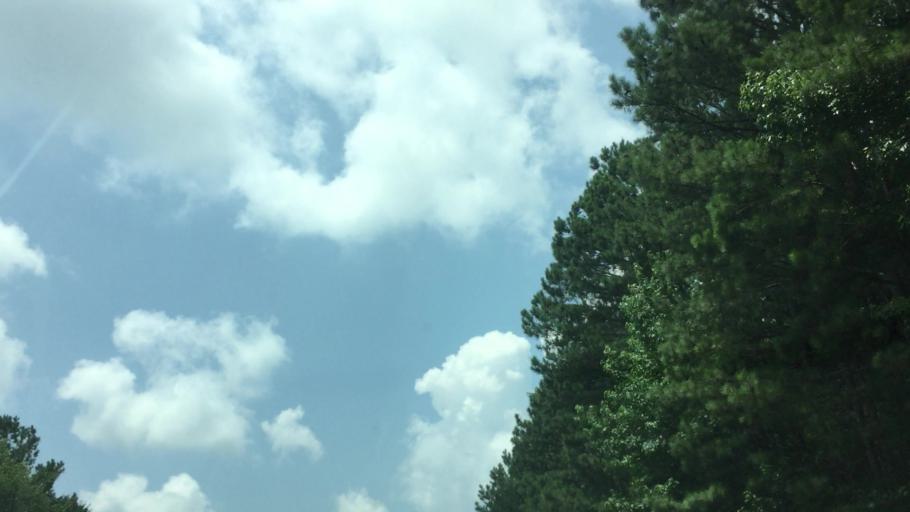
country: US
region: Georgia
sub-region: Fulton County
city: Chattahoochee Hills
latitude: 33.5637
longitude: -84.7533
